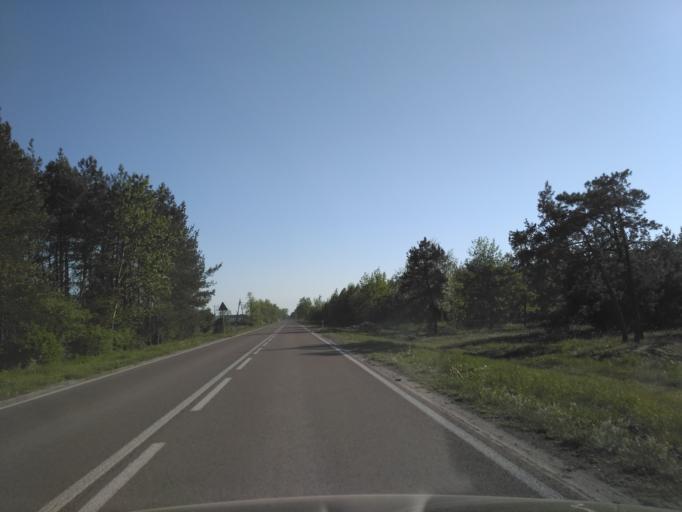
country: PL
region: Lublin Voivodeship
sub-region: Powiat swidnicki
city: Trawniki
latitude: 51.1700
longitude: 23.0355
